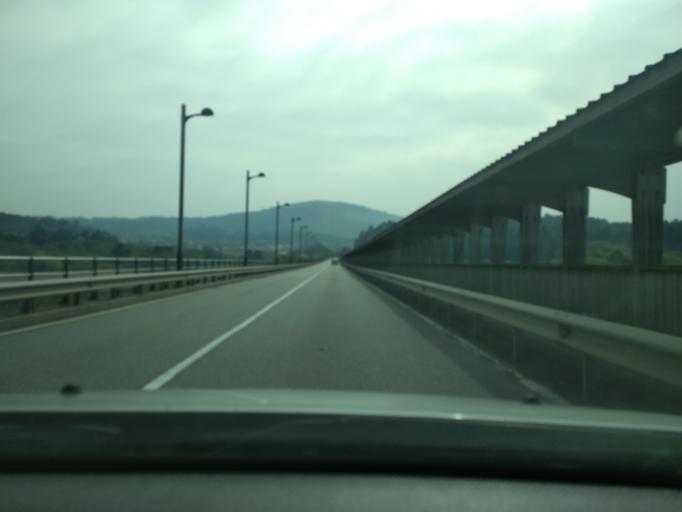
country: ES
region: Galicia
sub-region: Provincia de Pontevedra
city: Catoira
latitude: 42.6771
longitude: -8.7259
